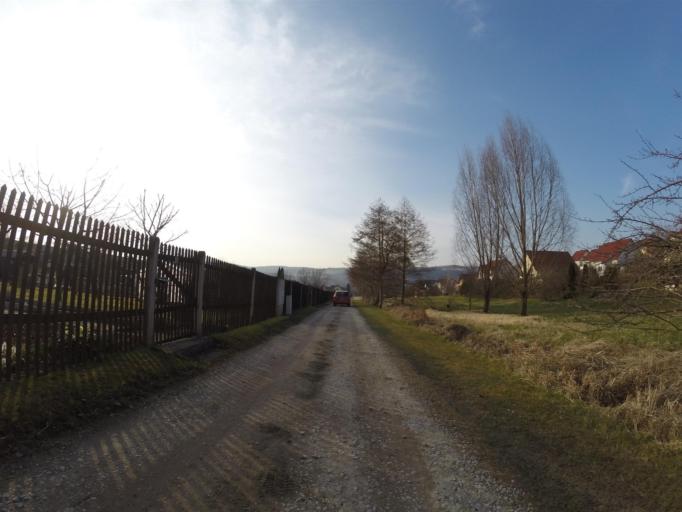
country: DE
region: Thuringia
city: Golmsdorf
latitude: 50.9509
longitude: 11.6403
